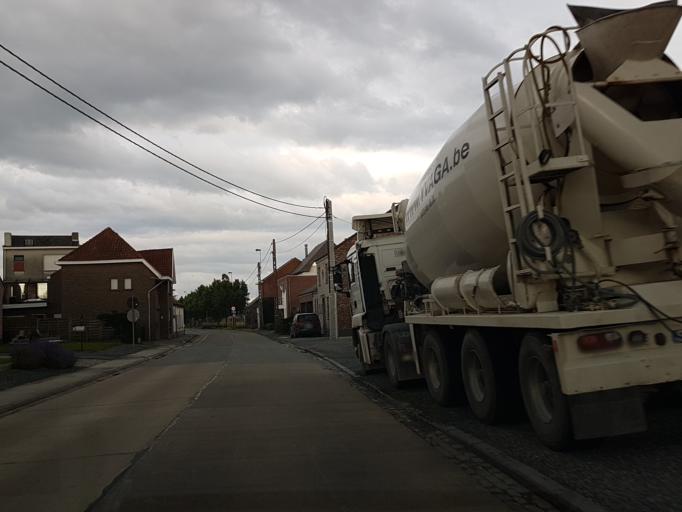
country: BE
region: Flanders
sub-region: Provincie Vlaams-Brabant
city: Opwijk
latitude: 50.9927
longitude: 4.1810
